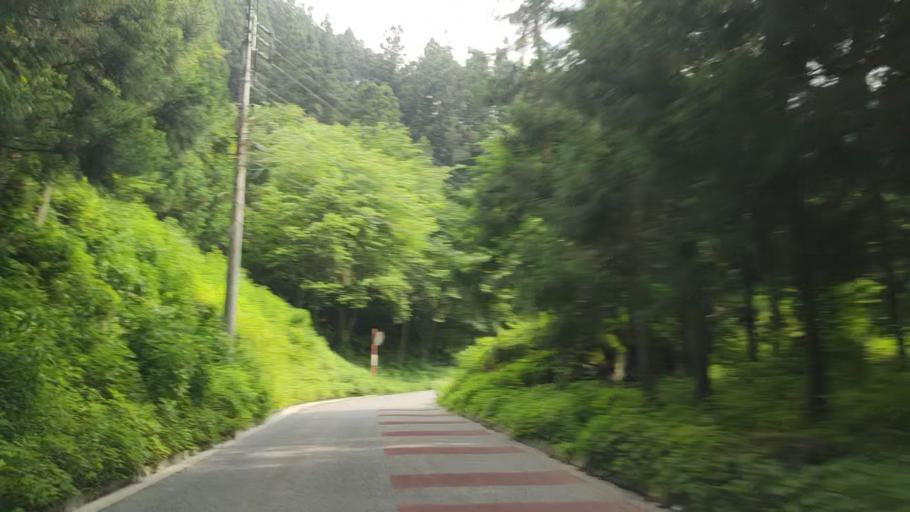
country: JP
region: Gunma
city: Tomioka
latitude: 36.1447
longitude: 138.7324
